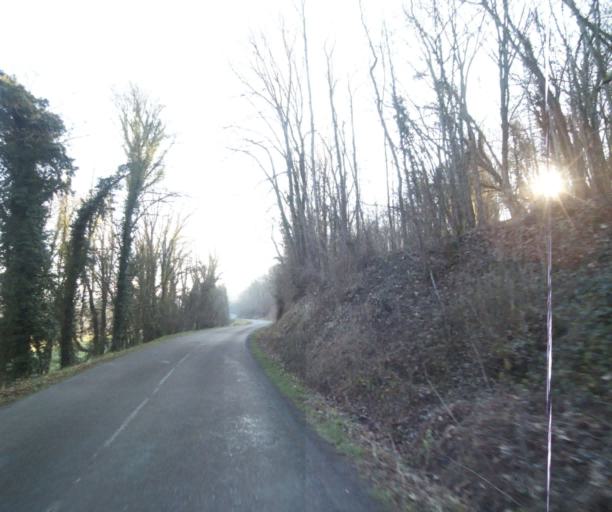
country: FR
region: Champagne-Ardenne
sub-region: Departement de la Haute-Marne
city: Bienville
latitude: 48.5703
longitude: 5.0786
